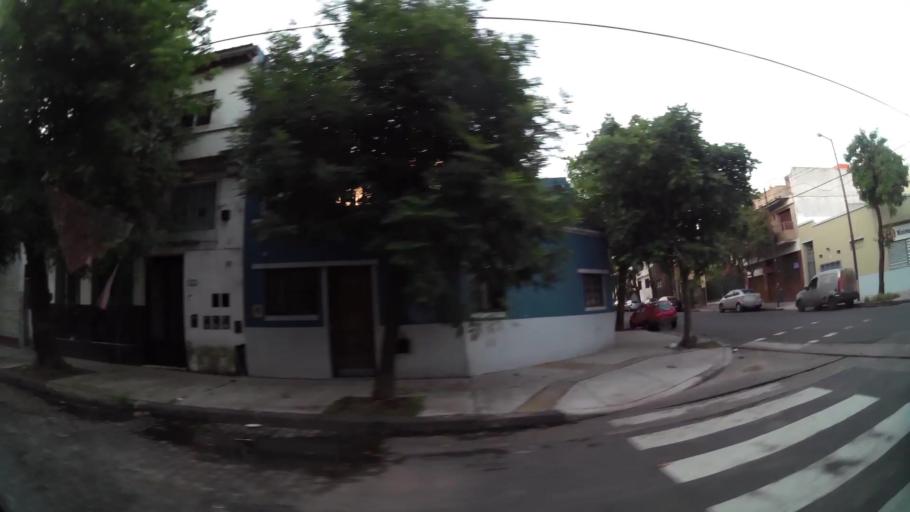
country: AR
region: Buenos Aires F.D.
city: Buenos Aires
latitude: -34.6344
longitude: -58.4194
